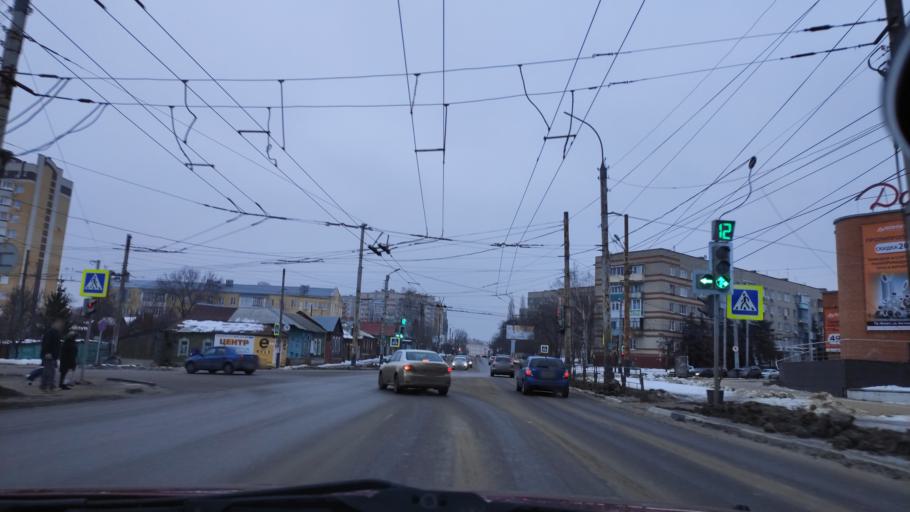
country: RU
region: Tambov
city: Tambov
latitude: 52.7011
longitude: 41.4616
